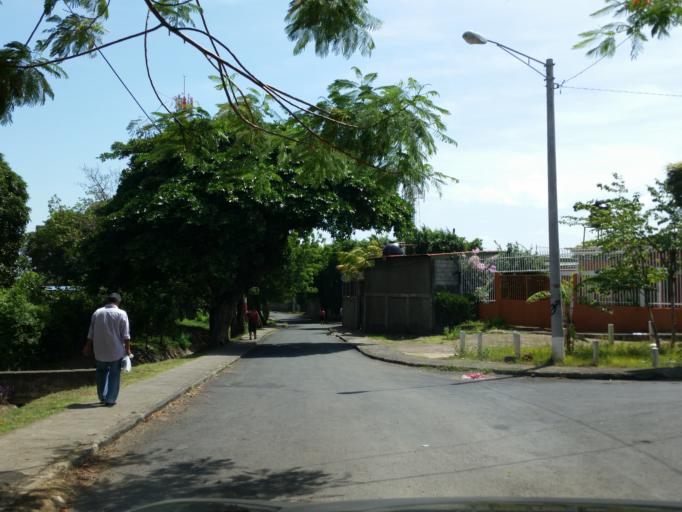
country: NI
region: Managua
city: Managua
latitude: 12.1118
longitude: -86.2500
